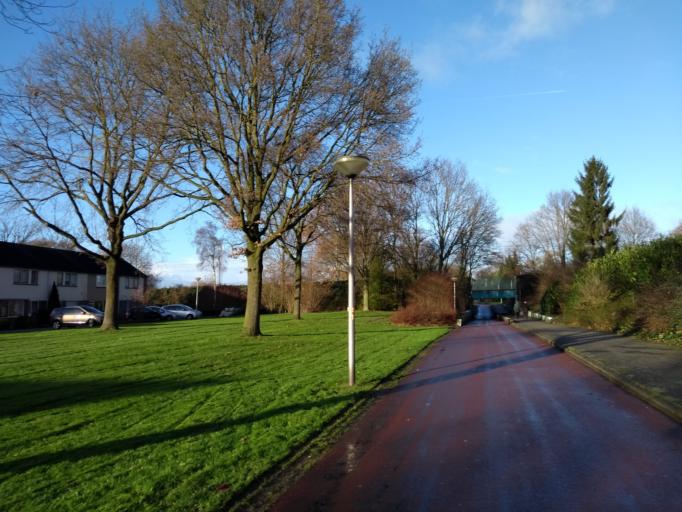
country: NL
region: Overijssel
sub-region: Gemeente Wierden
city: Wierden
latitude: 52.3612
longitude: 6.6009
